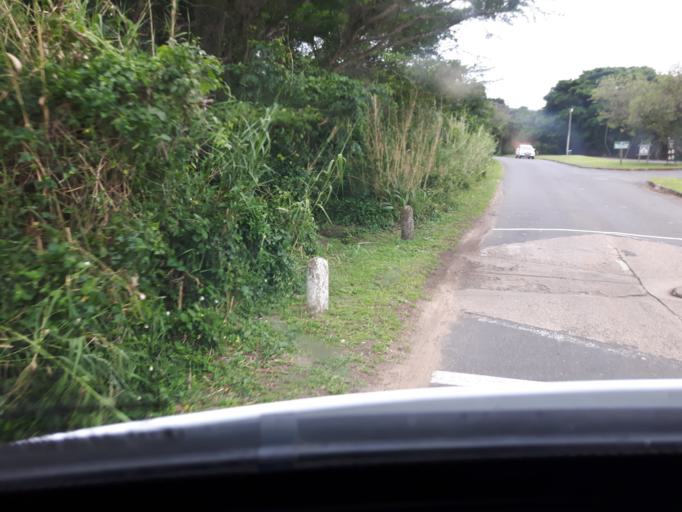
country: ZA
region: KwaZulu-Natal
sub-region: uMkhanyakude District Municipality
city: Mtubatuba
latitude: -28.3872
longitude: 32.4115
